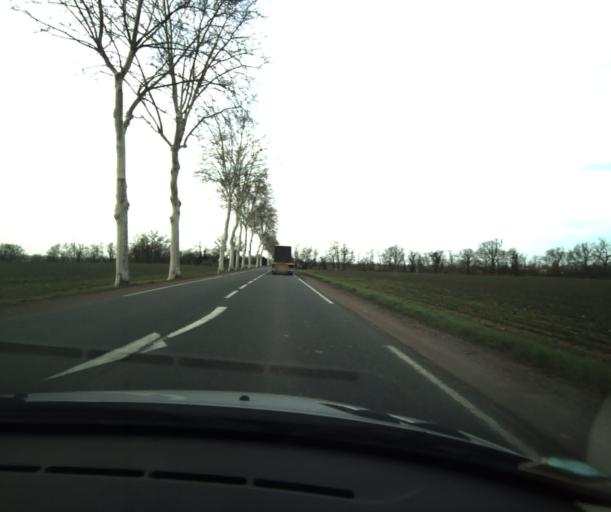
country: FR
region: Midi-Pyrenees
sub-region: Departement du Tarn-et-Garonne
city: Saint-Porquier
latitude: 44.0153
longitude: 1.1660
